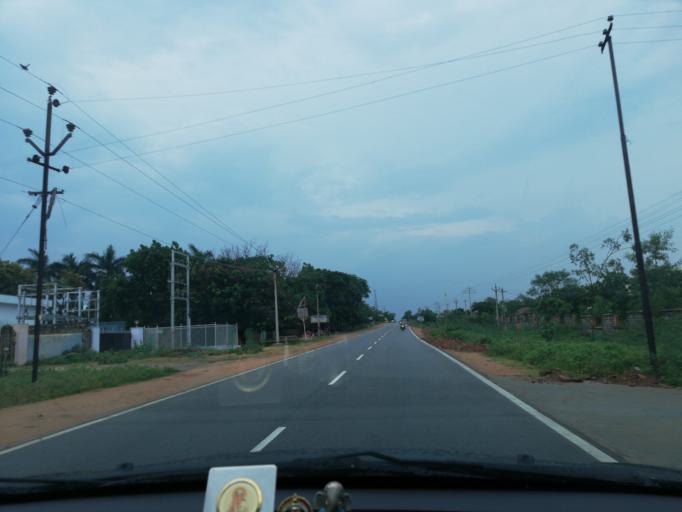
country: IN
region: Andhra Pradesh
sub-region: Guntur
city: Macherla
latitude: 16.6142
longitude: 79.2970
